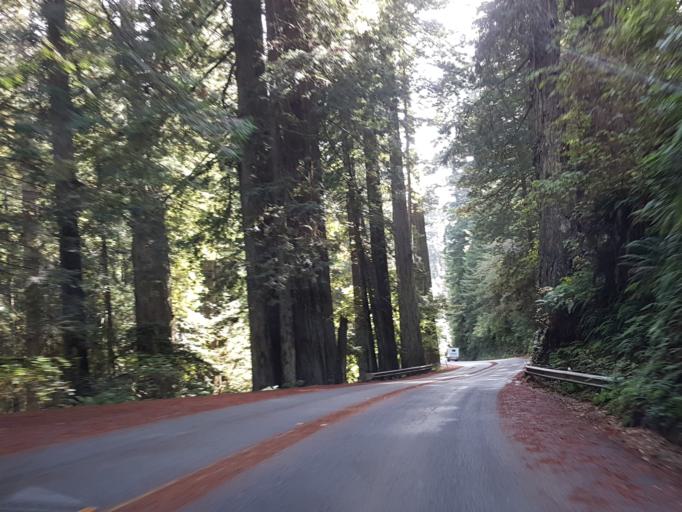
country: US
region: California
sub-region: Del Norte County
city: Bertsch-Oceanview
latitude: 41.4441
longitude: -124.0411
